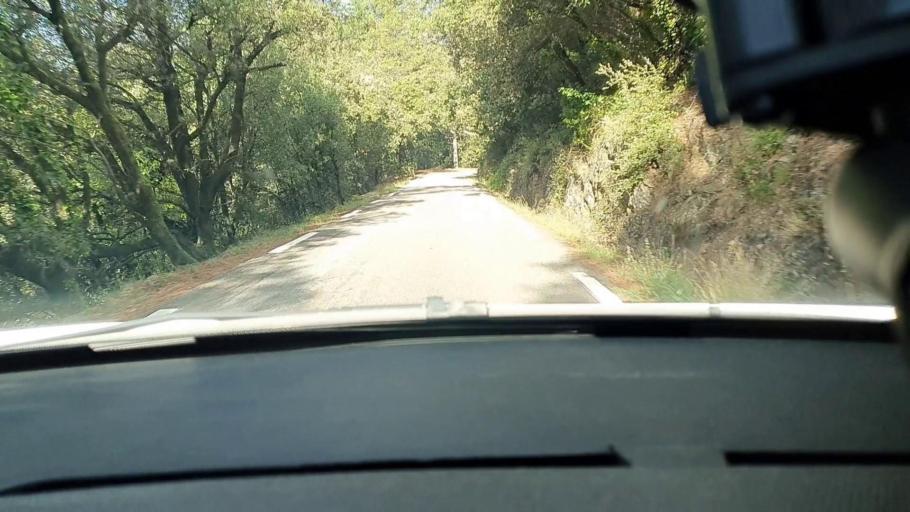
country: FR
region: Languedoc-Roussillon
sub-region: Departement du Gard
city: Besseges
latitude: 44.3596
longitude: 4.0095
